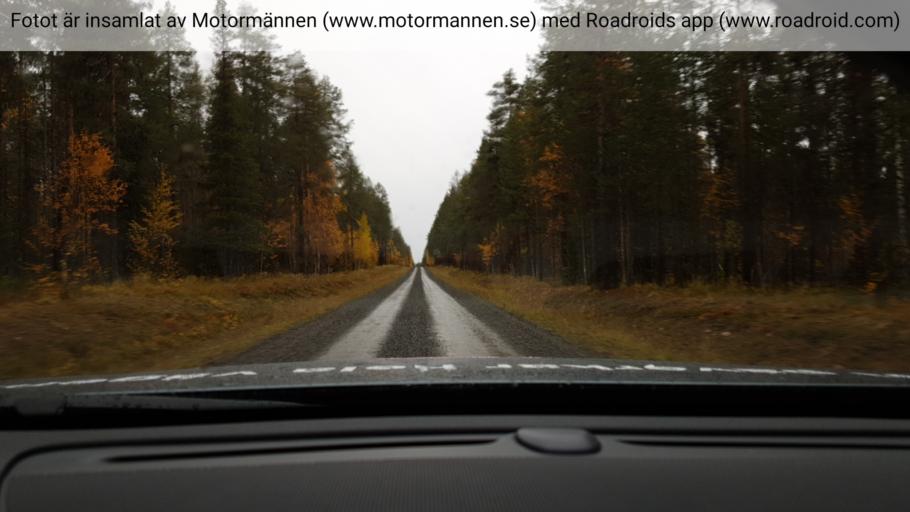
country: SE
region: Norrbotten
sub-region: Pajala Kommun
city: Pajala
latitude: 66.9843
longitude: 22.8730
